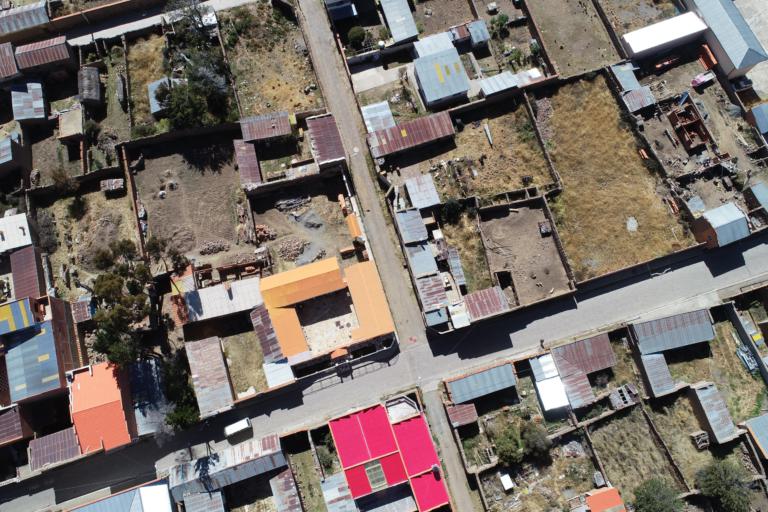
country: BO
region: La Paz
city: Achacachi
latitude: -15.8984
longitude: -68.9049
